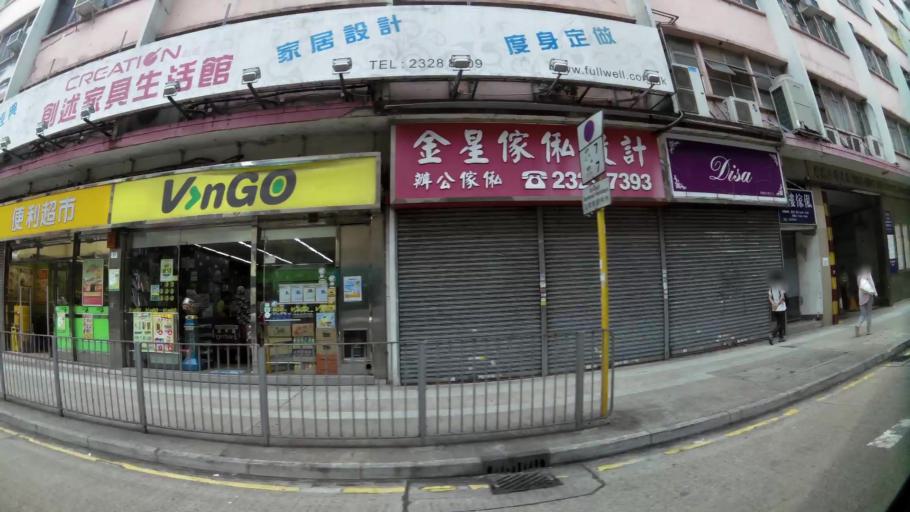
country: HK
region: Wong Tai Sin
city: Wong Tai Sin
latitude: 22.3360
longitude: 114.1965
